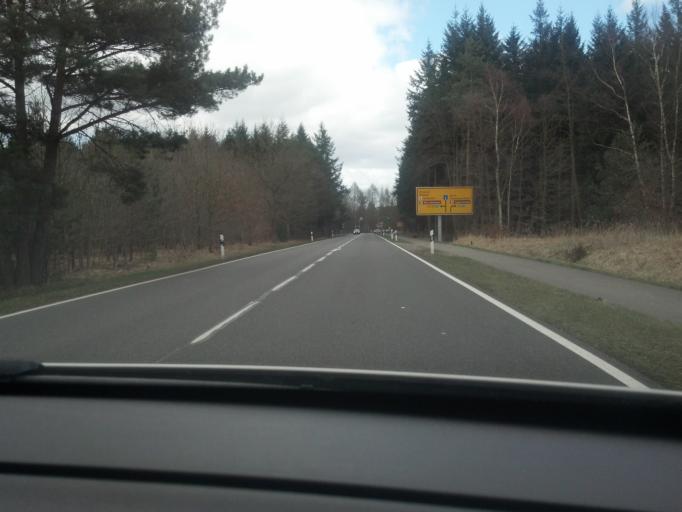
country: DE
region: Mecklenburg-Vorpommern
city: Neustrelitz
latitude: 53.3034
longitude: 13.0999
